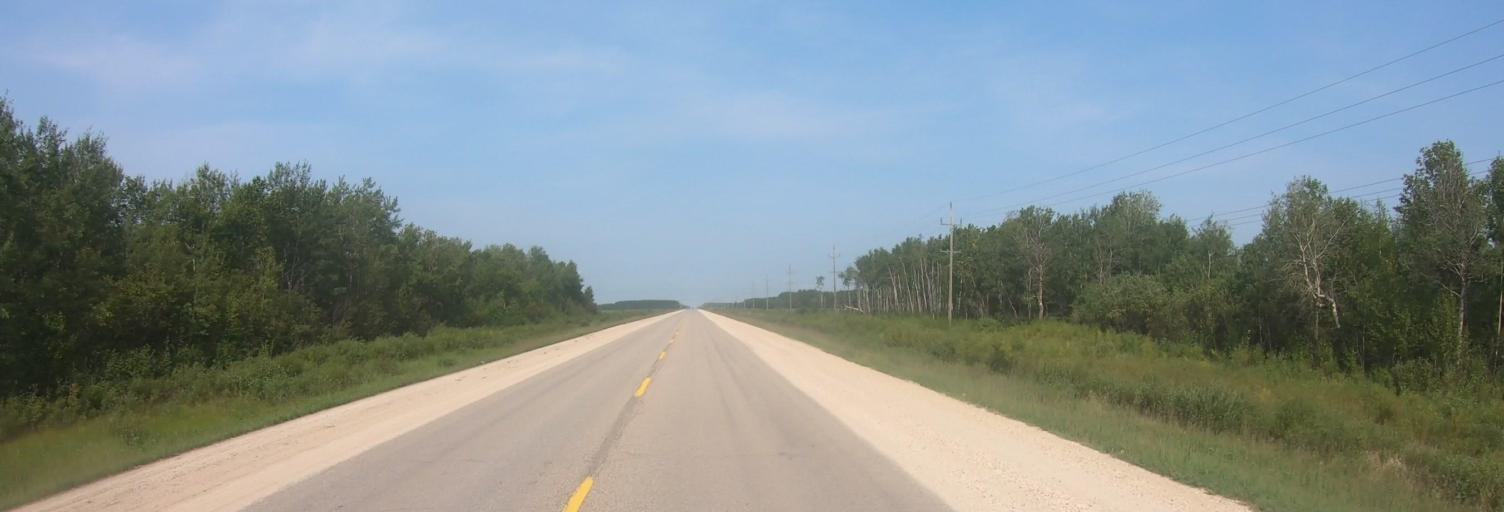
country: CA
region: Manitoba
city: La Broquerie
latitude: 49.2954
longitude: -96.5346
